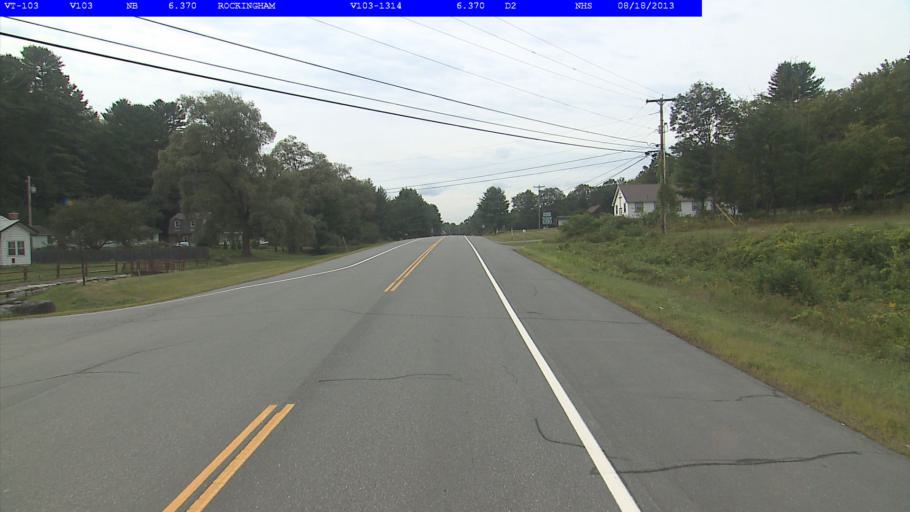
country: US
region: Vermont
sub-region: Windsor County
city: Chester
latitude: 43.2312
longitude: -72.5477
